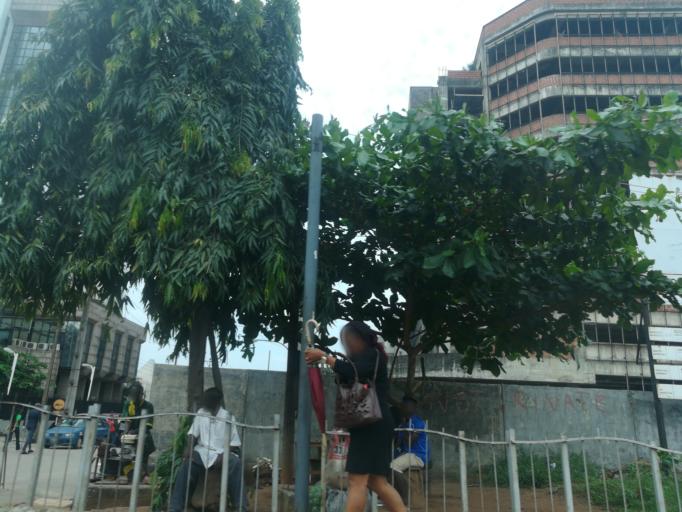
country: NG
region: Lagos
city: Ikeja
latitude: 6.5863
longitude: 3.3576
